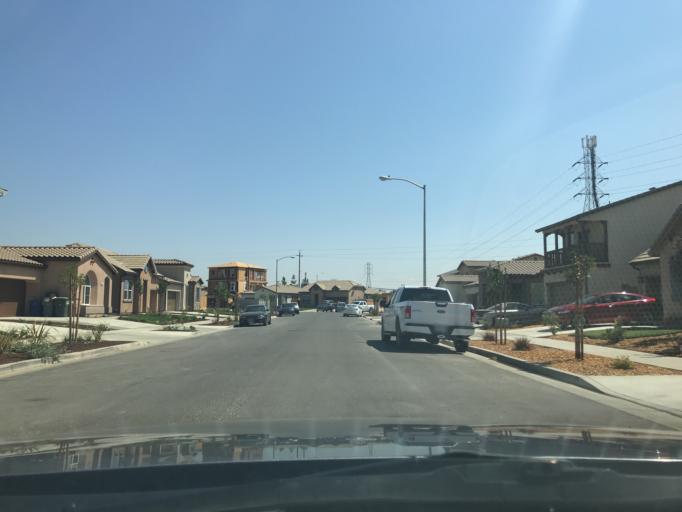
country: US
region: California
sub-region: Merced County
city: Merced
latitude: 37.3477
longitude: -120.4706
